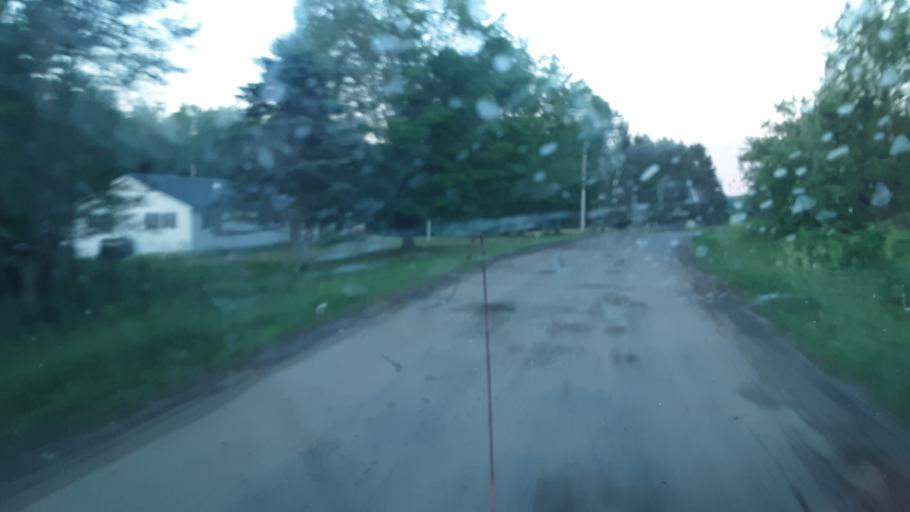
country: US
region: Maine
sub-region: Aroostook County
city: Caribou
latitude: 46.8716
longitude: -68.1220
